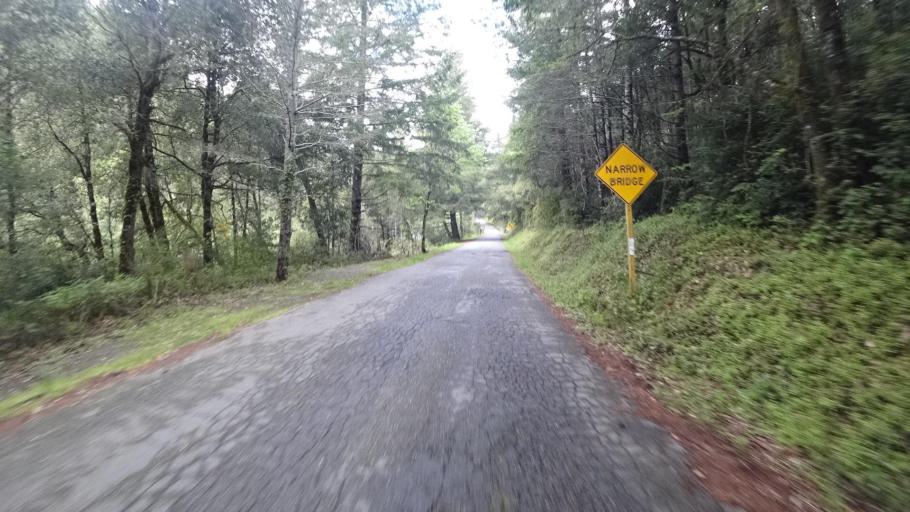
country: US
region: California
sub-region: Humboldt County
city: Blue Lake
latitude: 40.7634
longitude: -123.8883
